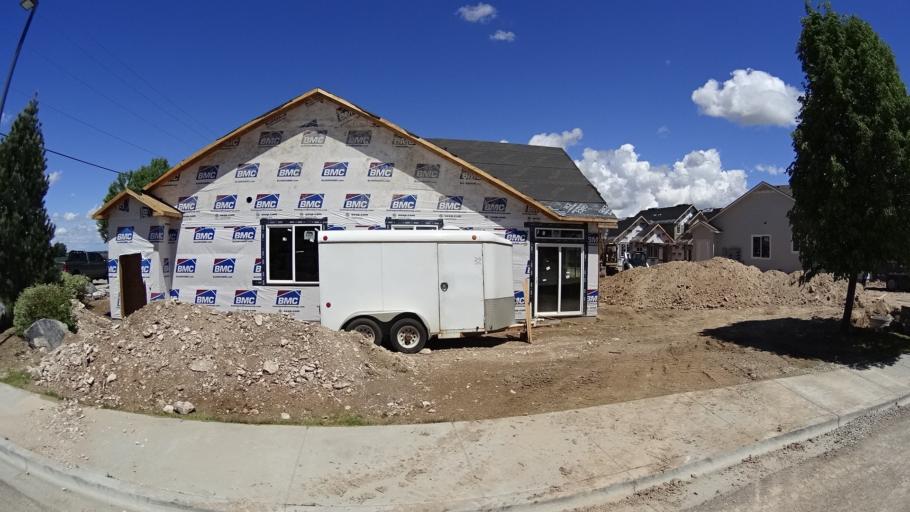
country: US
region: Idaho
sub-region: Ada County
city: Kuna
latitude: 43.5131
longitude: -116.4333
